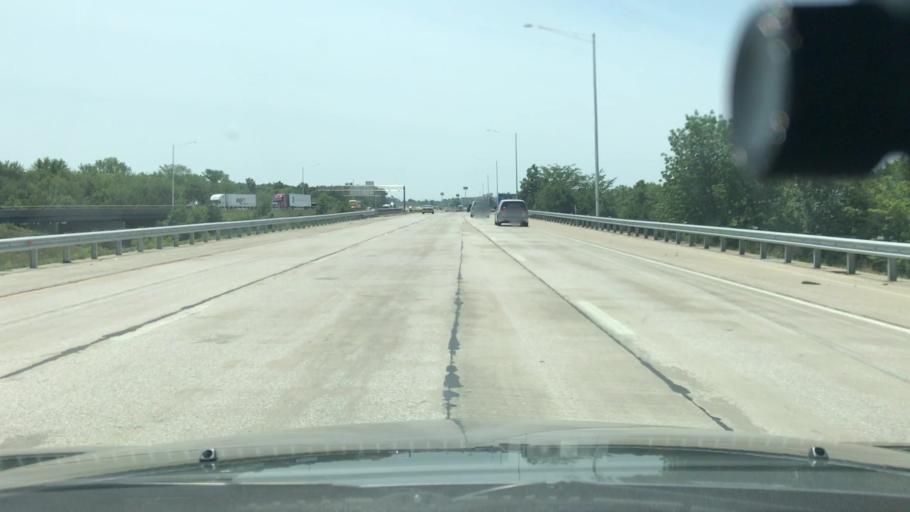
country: US
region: Illinois
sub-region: Jefferson County
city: Mount Vernon
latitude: 38.3291
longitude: -88.9564
